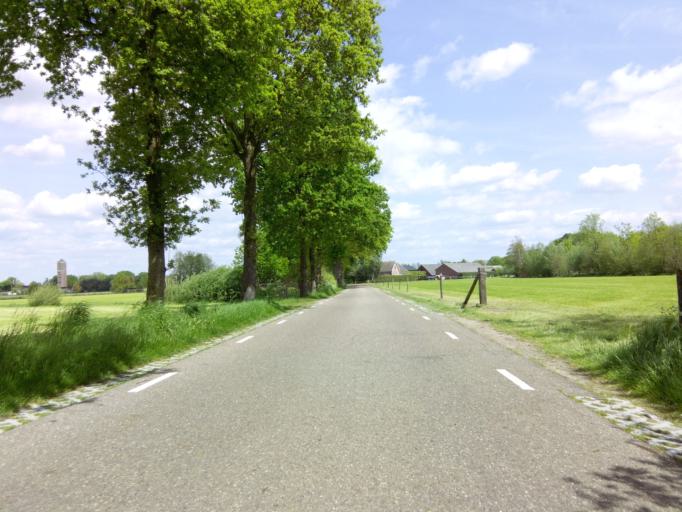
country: NL
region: Utrecht
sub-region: Gemeente Woudenberg
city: Woudenberg
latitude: 52.0741
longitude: 5.4575
